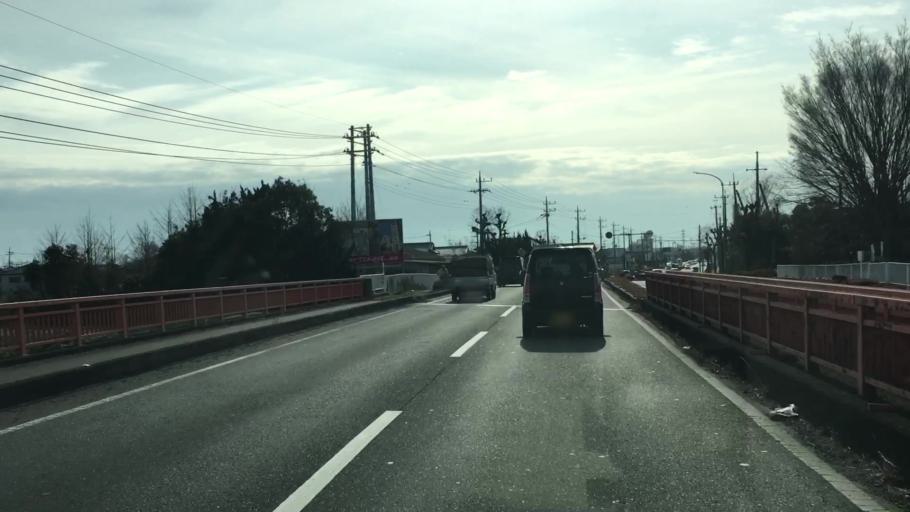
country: JP
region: Saitama
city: Menuma
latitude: 36.2080
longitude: 139.3706
